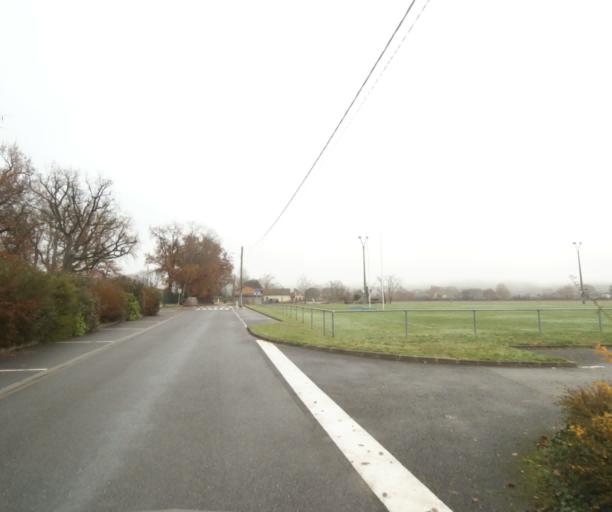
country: FR
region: Midi-Pyrenees
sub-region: Departement de la Haute-Garonne
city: Villemur-sur-Tarn
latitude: 43.8525
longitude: 1.5009
